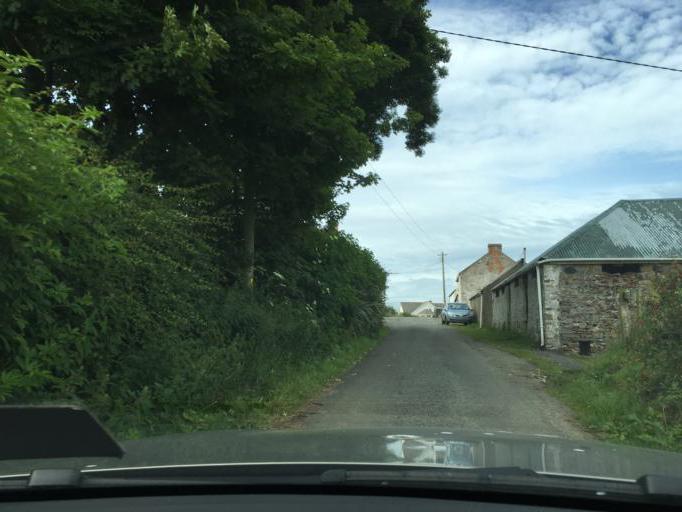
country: IE
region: Ulster
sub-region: County Donegal
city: Carndonagh
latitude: 55.3265
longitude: -7.3129
